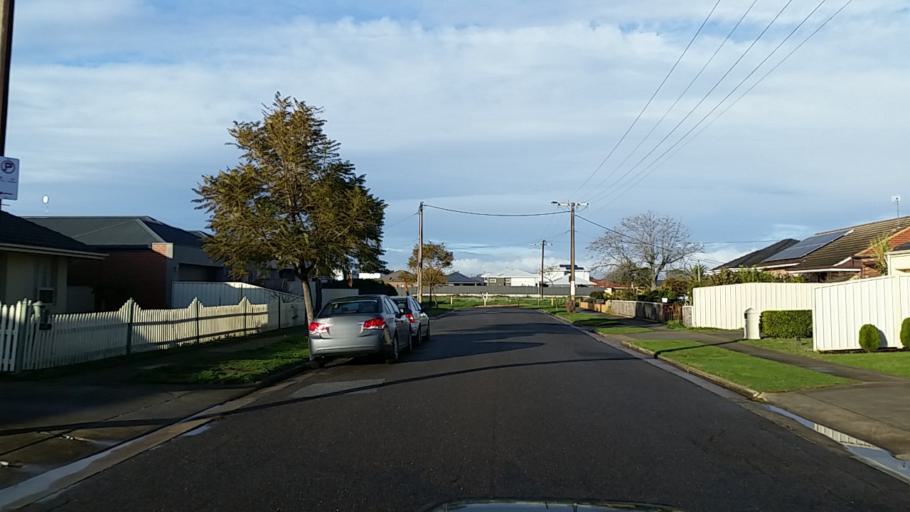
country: AU
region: South Australia
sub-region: Charles Sturt
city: Findon
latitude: -34.9032
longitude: 138.5338
